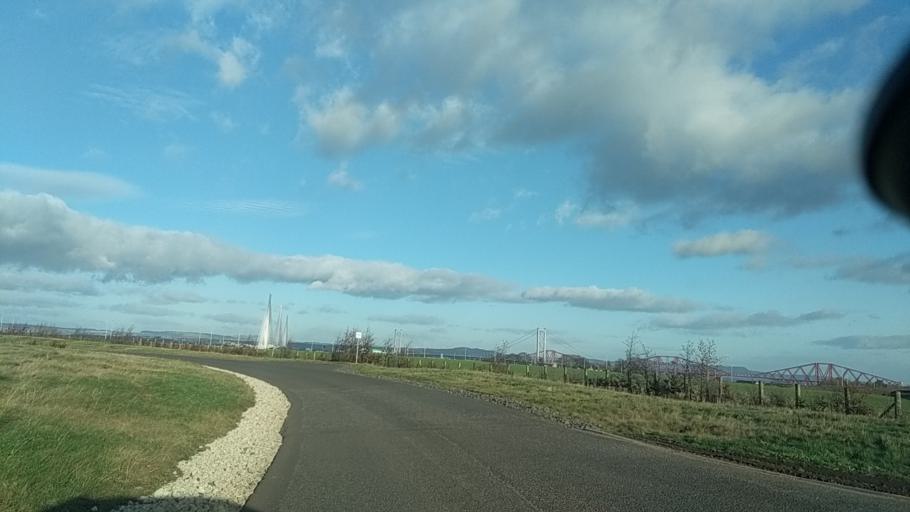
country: GB
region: Scotland
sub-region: Edinburgh
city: Queensferry
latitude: 55.9816
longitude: -3.4249
